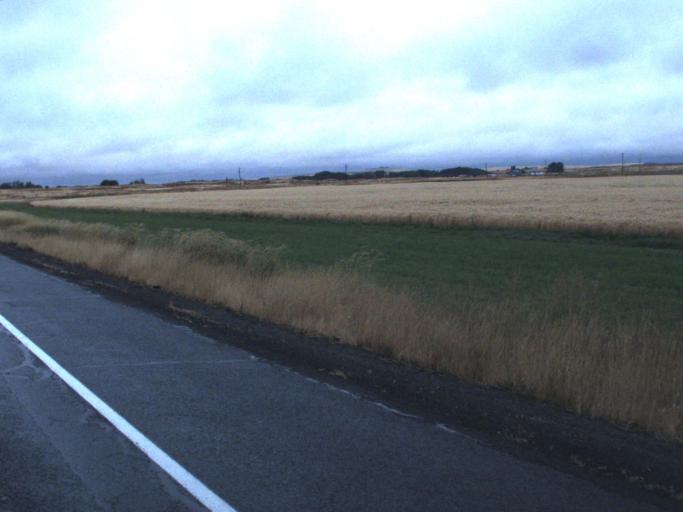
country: US
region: Washington
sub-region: Spokane County
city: Medical Lake
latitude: 47.6621
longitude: -117.8369
